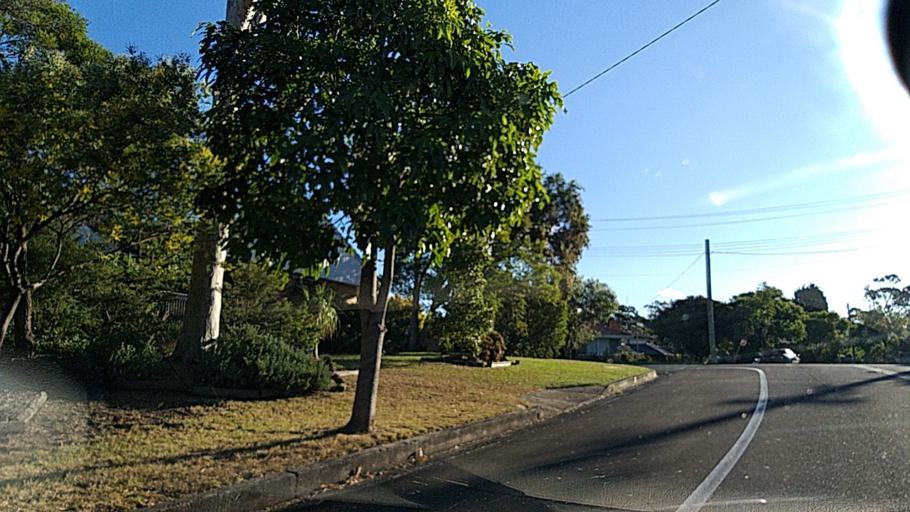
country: AU
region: New South Wales
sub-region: Wollongong
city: Mount Keira
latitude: -34.4312
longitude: 150.8489
